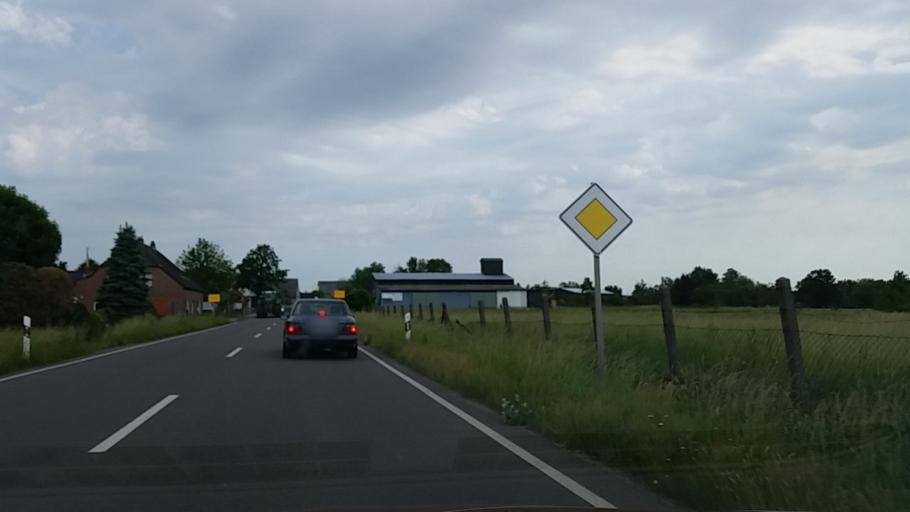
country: DE
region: Lower Saxony
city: Parsau
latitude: 52.5303
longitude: 10.8907
